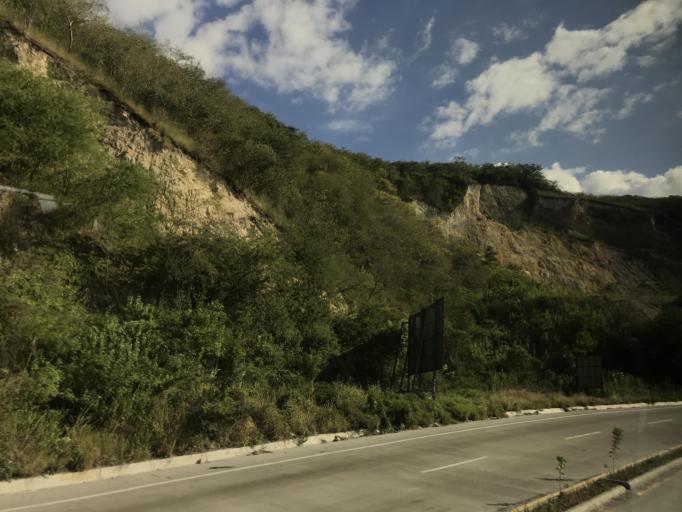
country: GT
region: El Progreso
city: Guastatoya
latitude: 14.8483
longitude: -90.1217
